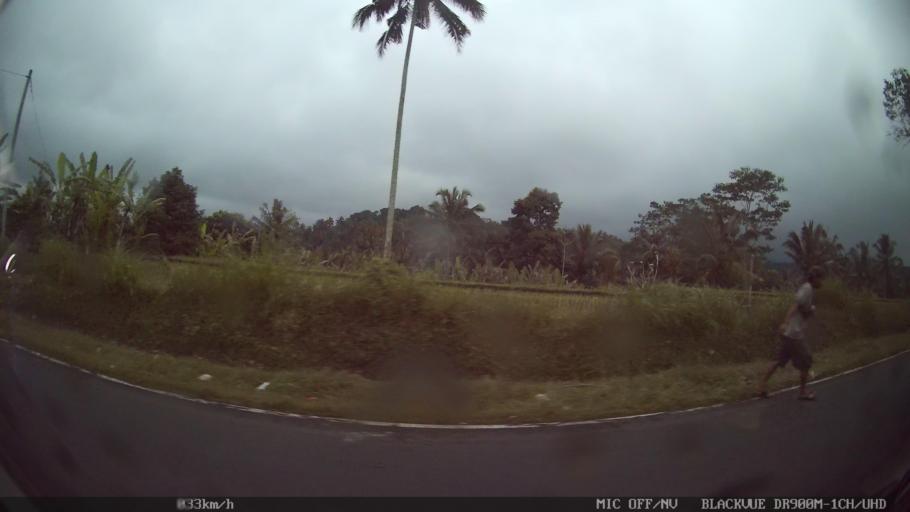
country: ID
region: Bali
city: Banjar Ponggang
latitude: -8.3953
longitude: 115.2527
